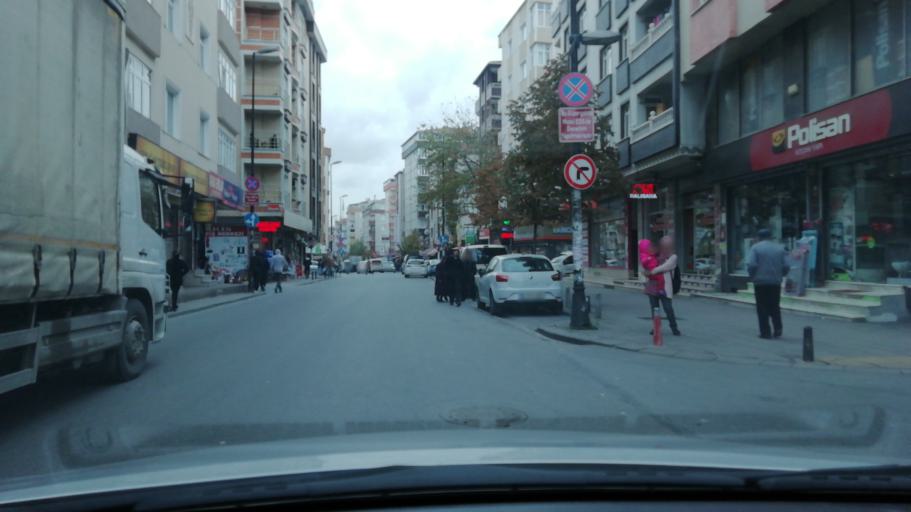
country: TR
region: Istanbul
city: Bahcelievler
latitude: 41.0088
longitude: 28.8388
